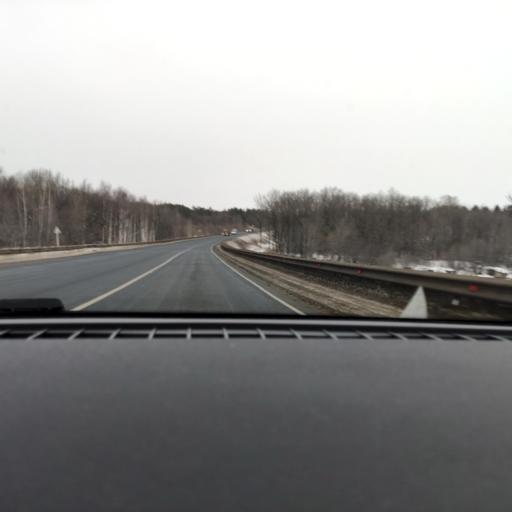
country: RU
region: Samara
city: Novosemeykino
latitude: 53.3572
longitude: 50.4432
